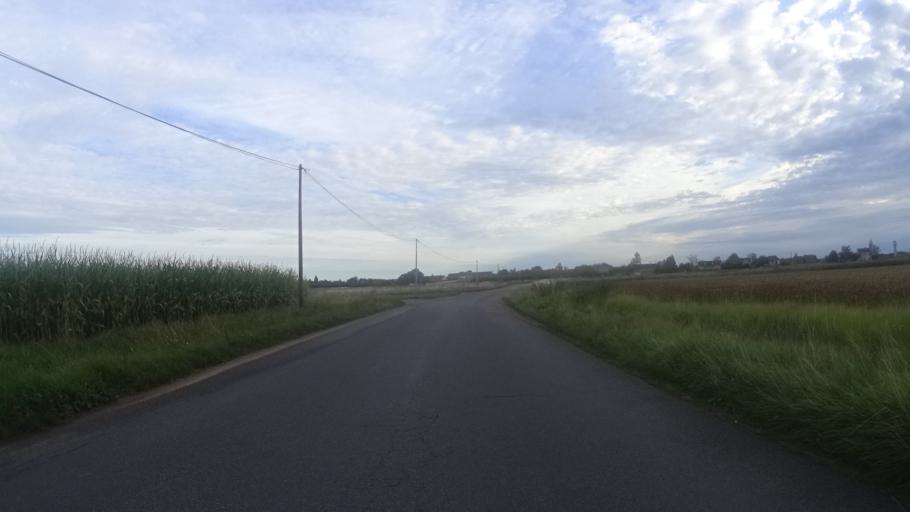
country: FR
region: Centre
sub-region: Departement du Loiret
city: Saint-Benoit-sur-Loire
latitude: 47.7974
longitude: 2.3113
